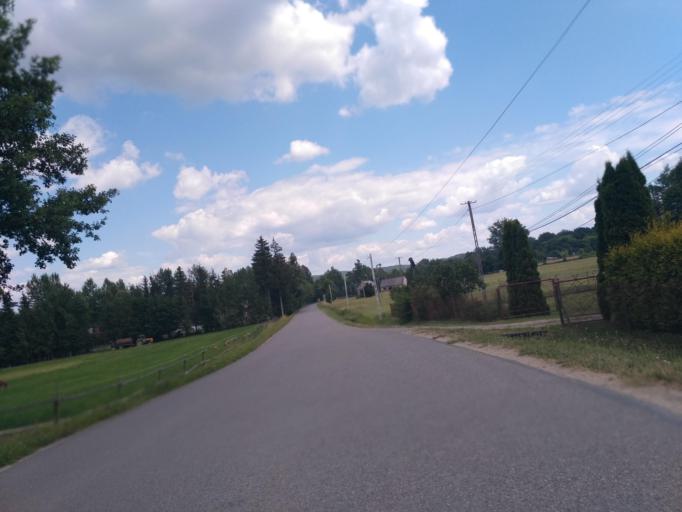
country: PL
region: Subcarpathian Voivodeship
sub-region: Powiat debicki
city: Brzostek
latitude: 49.8594
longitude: 21.4357
